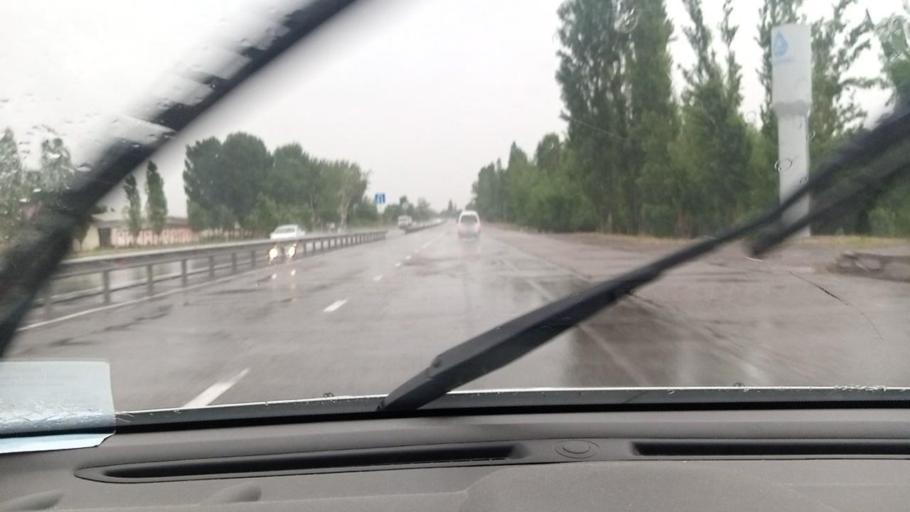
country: UZ
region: Toshkent
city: Ohangaron
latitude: 40.9087
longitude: 69.7624
